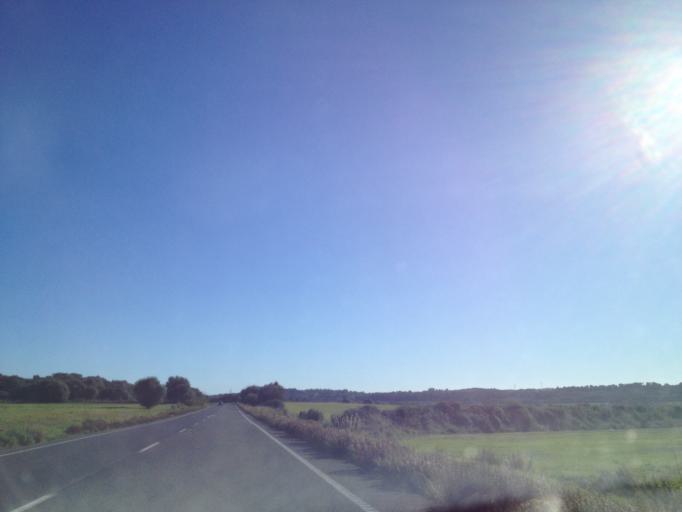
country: ES
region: Balearic Islands
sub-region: Illes Balears
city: Maria de la Salut
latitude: 39.6436
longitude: 3.0464
